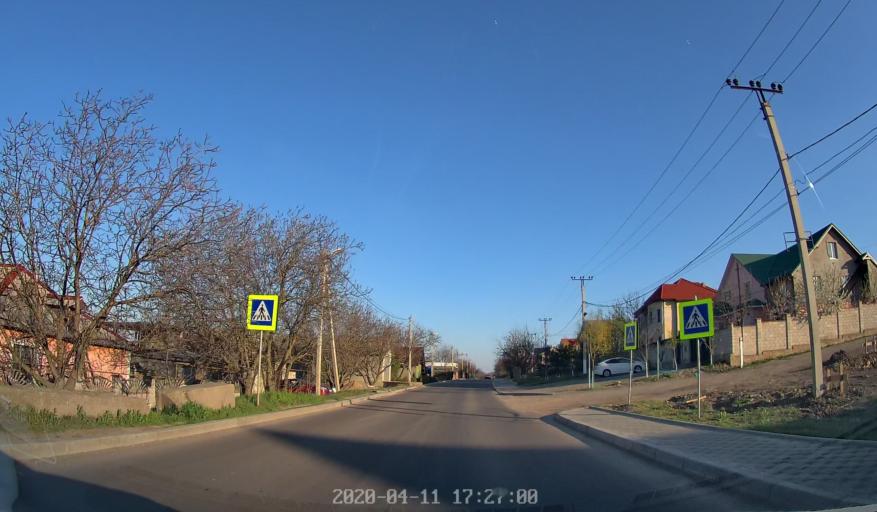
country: MD
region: Chisinau
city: Vatra
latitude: 47.0112
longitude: 28.7603
